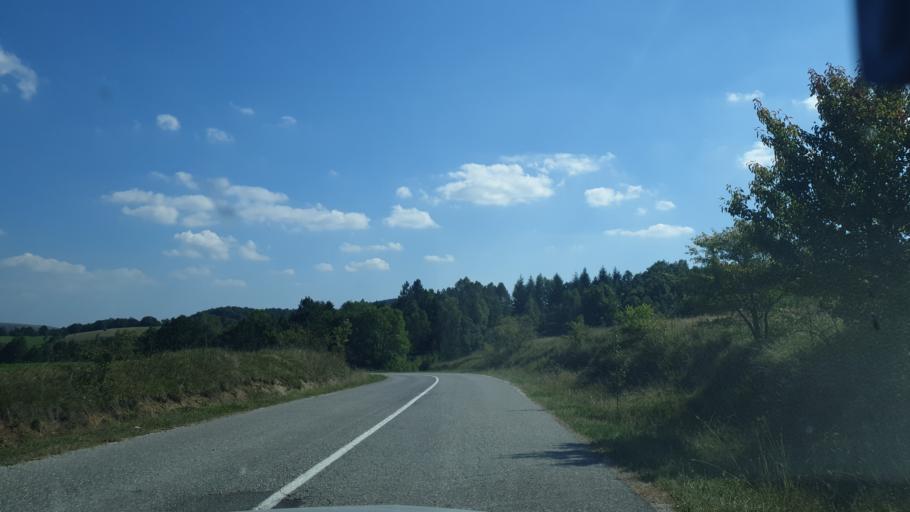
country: RS
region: Central Serbia
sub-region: Zlatiborski Okrug
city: Kosjeric
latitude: 44.0560
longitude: 20.0288
